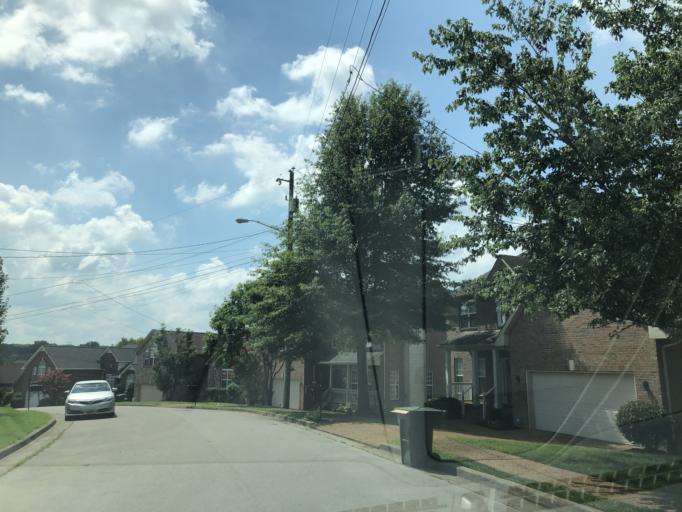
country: US
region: Tennessee
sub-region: Williamson County
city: Nolensville
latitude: 36.0140
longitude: -86.6958
